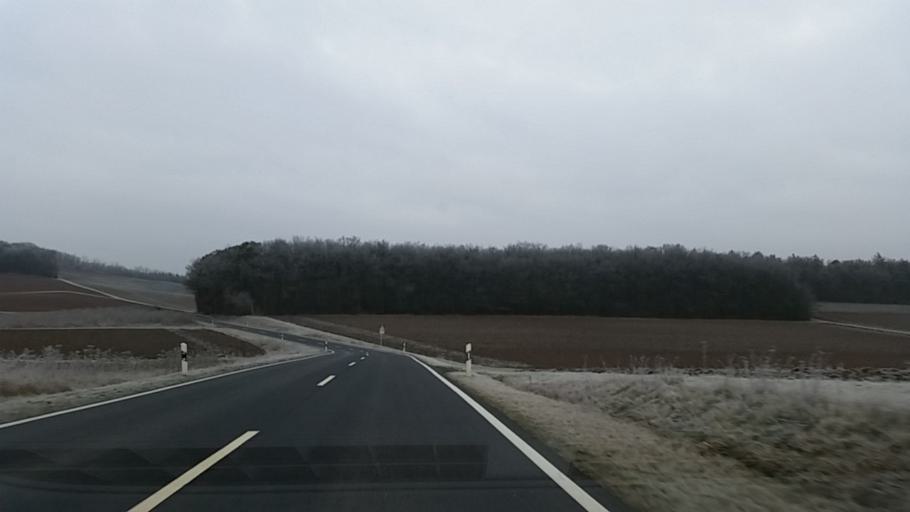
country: DE
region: Bavaria
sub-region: Regierungsbezirk Unterfranken
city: Fuchsstadt
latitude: 50.0587
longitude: 9.9191
